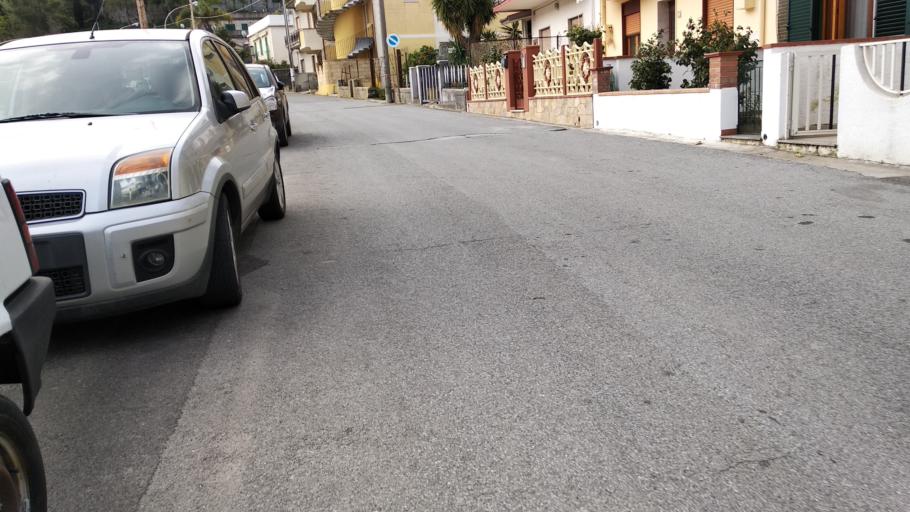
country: IT
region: Sicily
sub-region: Messina
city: Villafranca Tirrena
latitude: 38.2227
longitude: 15.4521
